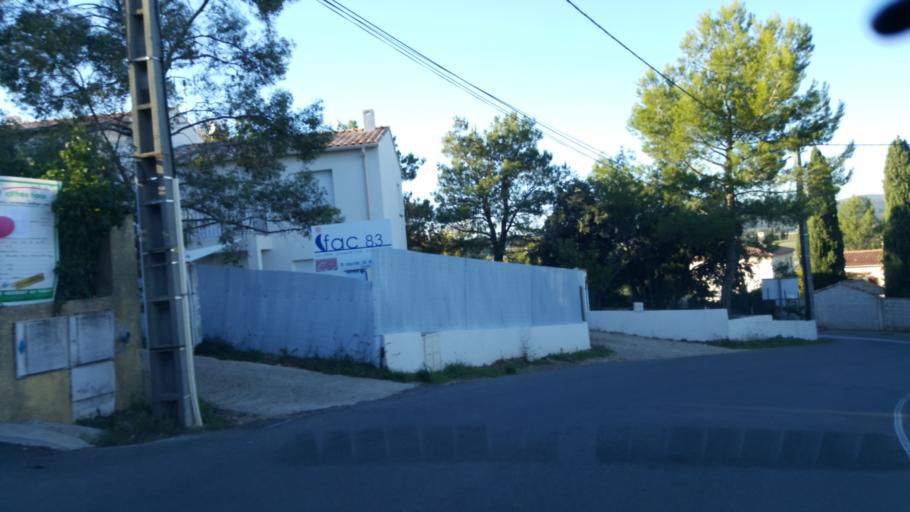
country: FR
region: Provence-Alpes-Cote d'Azur
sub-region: Departement du Var
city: Saint-Maximin-la-Sainte-Baume
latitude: 43.4519
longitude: 5.8507
